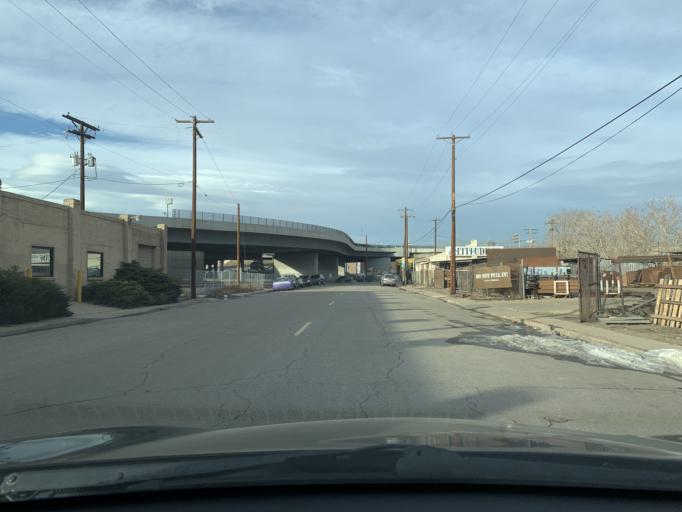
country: US
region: Colorado
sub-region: Denver County
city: Denver
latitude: 39.7387
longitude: -105.0123
